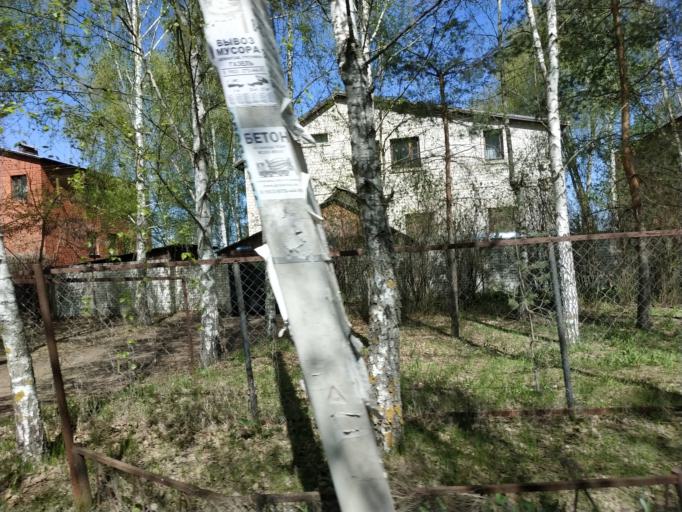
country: RU
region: Moskovskaya
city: Malyshevo
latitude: 55.4622
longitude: 38.3611
